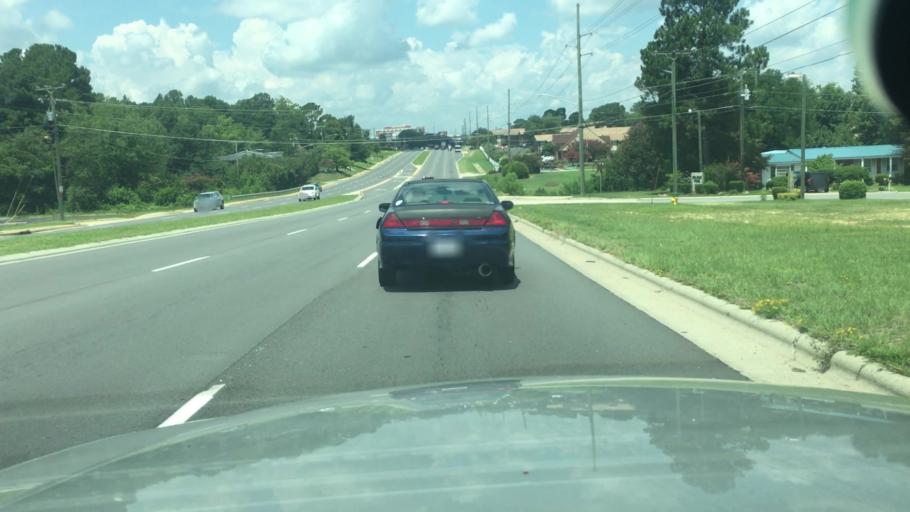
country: US
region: North Carolina
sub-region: Cumberland County
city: Fayetteville
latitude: 35.0241
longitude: -78.9237
